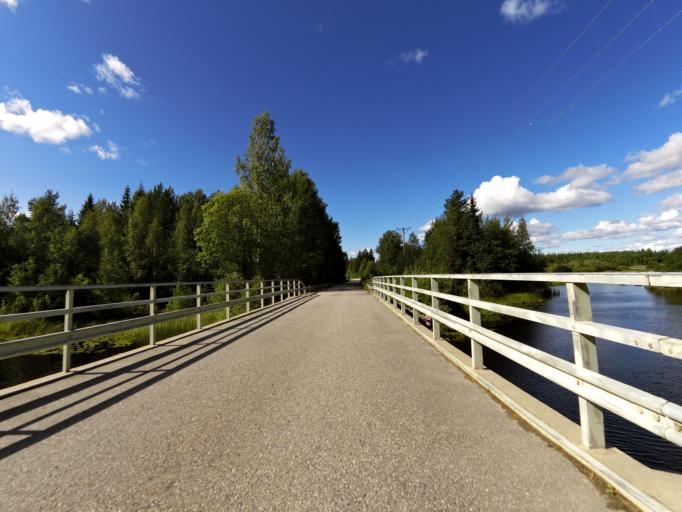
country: SE
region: Gaevleborg
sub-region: Gavle Kommun
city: Valbo
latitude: 60.7690
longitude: 16.9323
